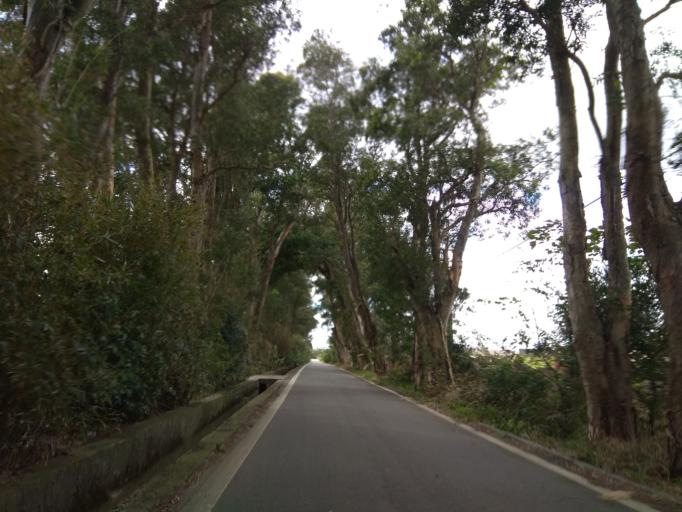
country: TW
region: Taiwan
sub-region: Hsinchu
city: Zhubei
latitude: 24.9742
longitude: 121.0861
